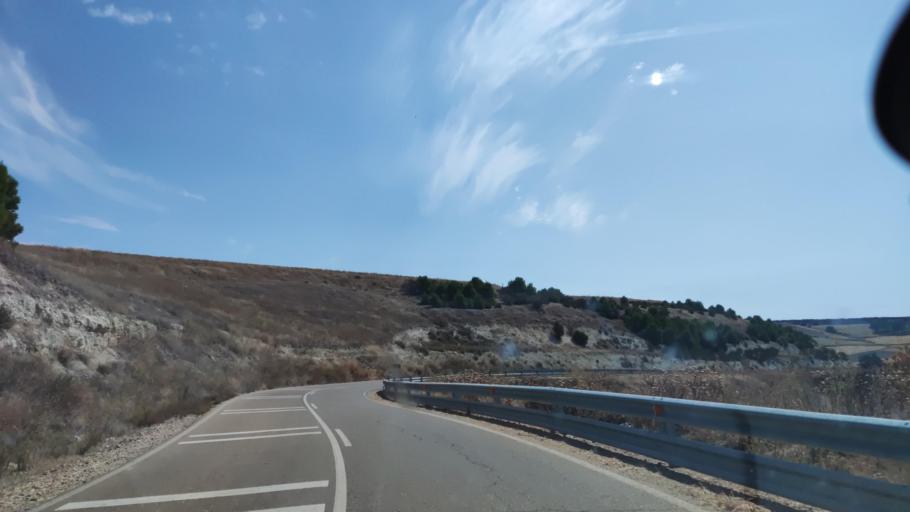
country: ES
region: Castille and Leon
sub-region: Provincia de Valladolid
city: Uruena
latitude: 41.7252
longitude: -5.1993
